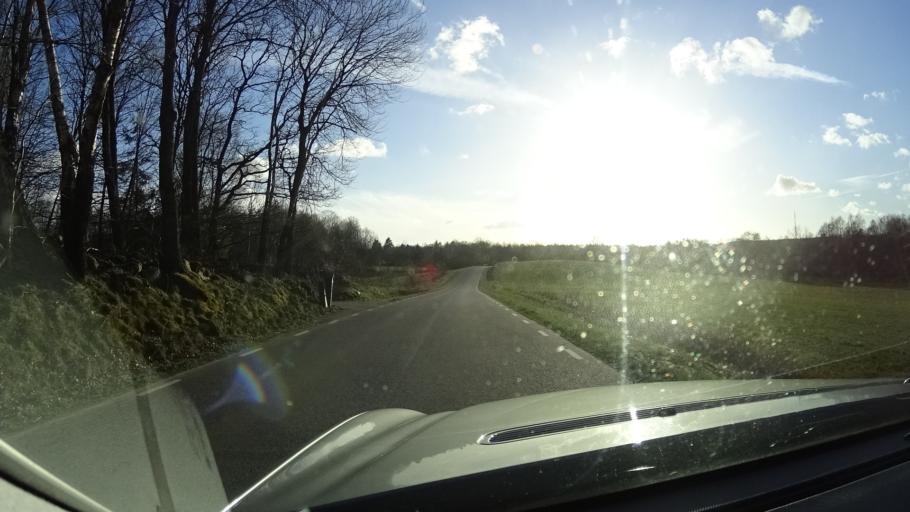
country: SE
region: Skane
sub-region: Hoors Kommun
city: Hoeoer
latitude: 55.9215
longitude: 13.5151
